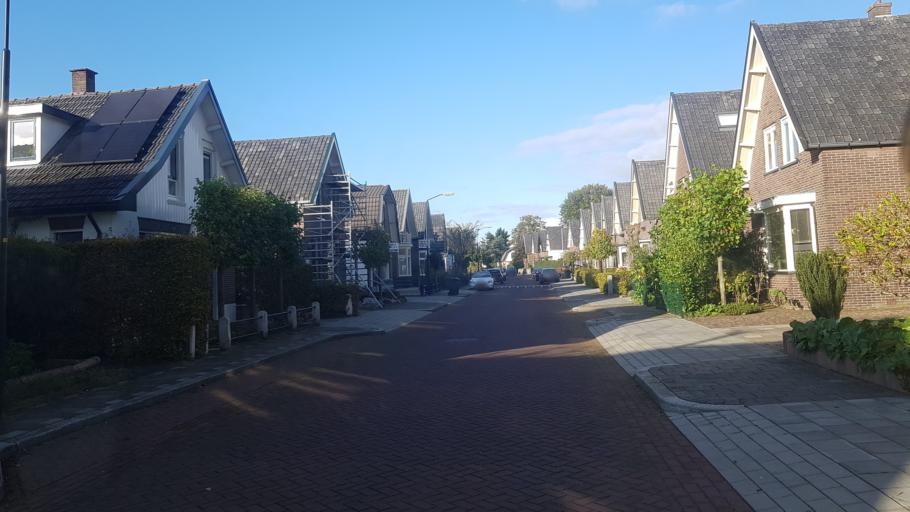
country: NL
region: Gelderland
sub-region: Gemeente Apeldoorn
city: Apeldoorn
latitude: 52.2075
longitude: 5.9453
